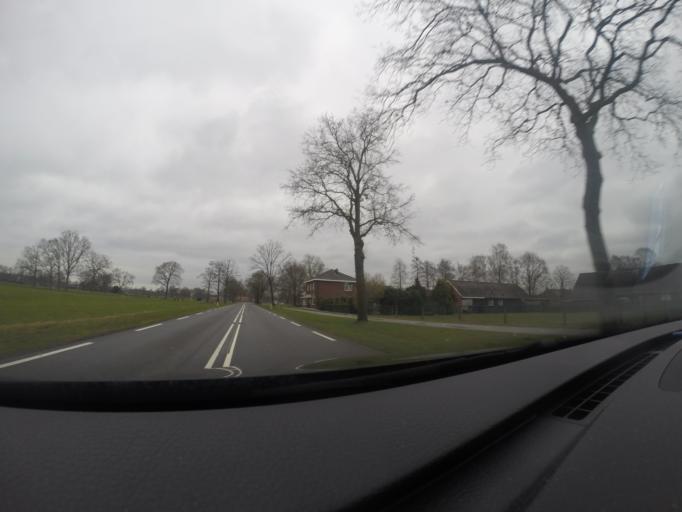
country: NL
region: Overijssel
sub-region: Gemeente Hof van Twente
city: Delden
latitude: 52.2370
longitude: 6.6912
